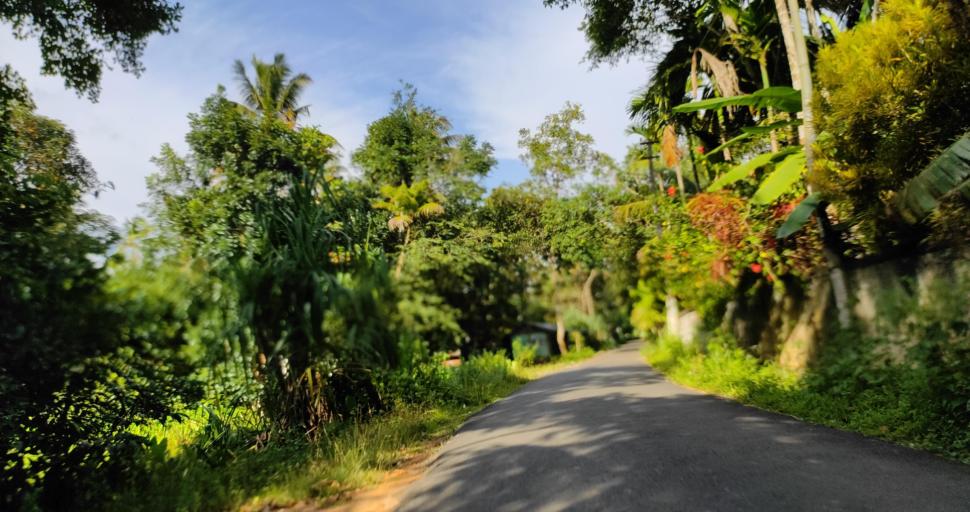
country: IN
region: Kerala
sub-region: Alappuzha
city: Shertallai
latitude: 9.6010
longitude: 76.3317
